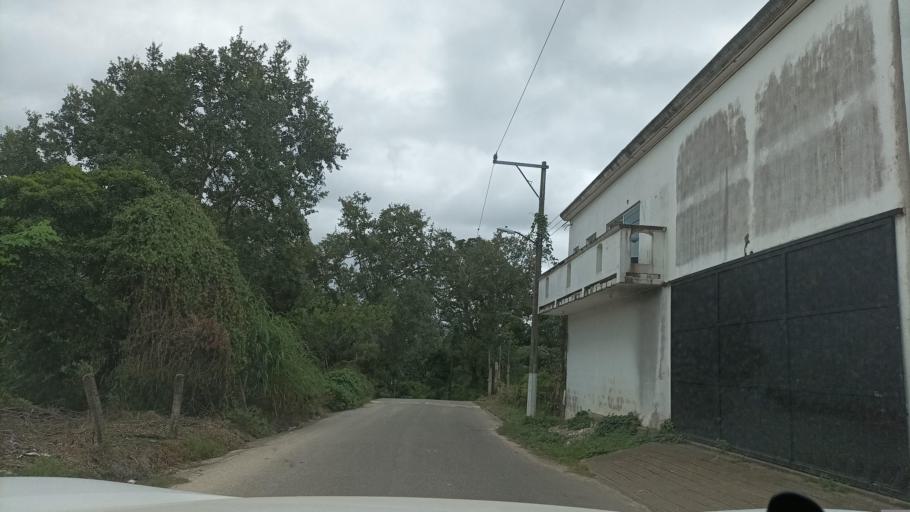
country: MX
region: Veracruz
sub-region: Cosoleacaque
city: Coacotla
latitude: 17.9496
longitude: -94.7111
